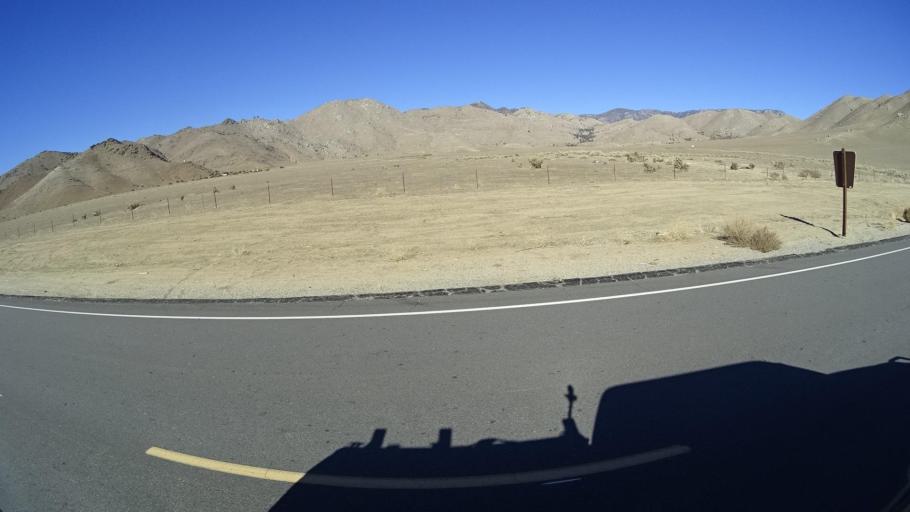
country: US
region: California
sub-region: Kern County
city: Weldon
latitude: 35.6782
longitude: -118.3660
